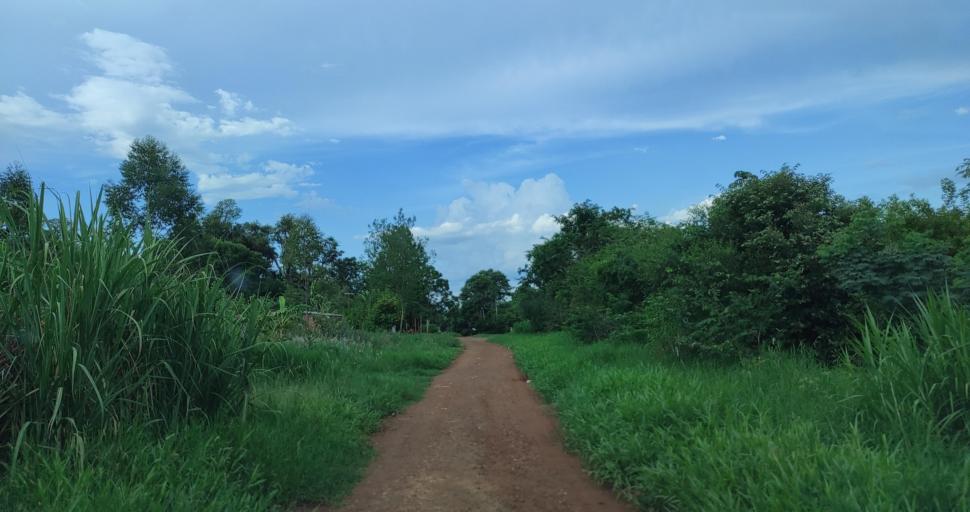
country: AR
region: Misiones
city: Gobernador Roca
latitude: -27.1879
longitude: -55.4692
